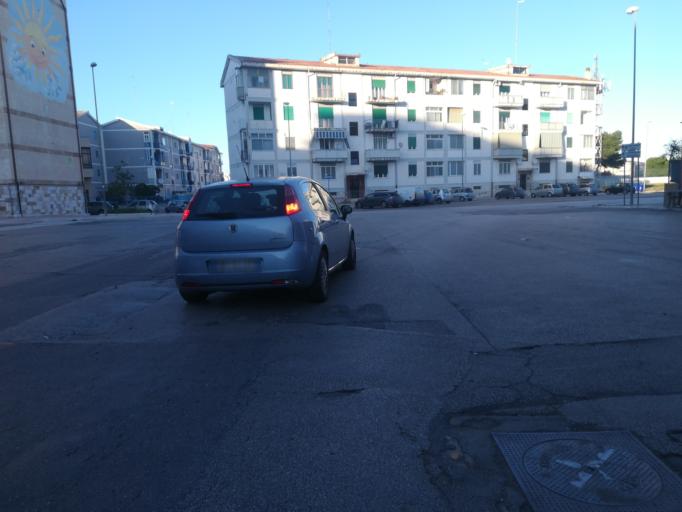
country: IT
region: Apulia
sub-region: Provincia di Bari
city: San Paolo
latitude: 41.1192
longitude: 16.7911
